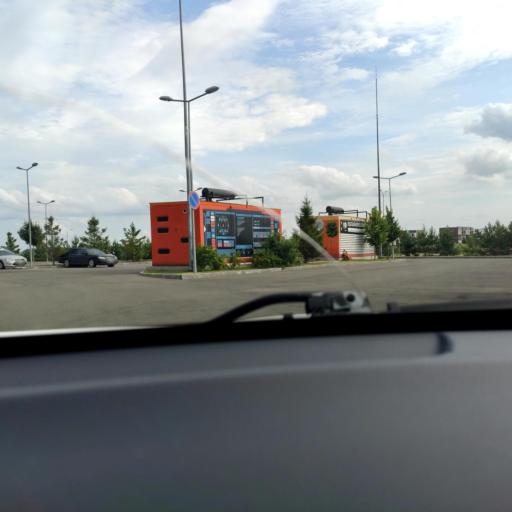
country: RU
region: Tatarstan
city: Sviyazhsk
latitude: 55.7515
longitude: 48.7512
